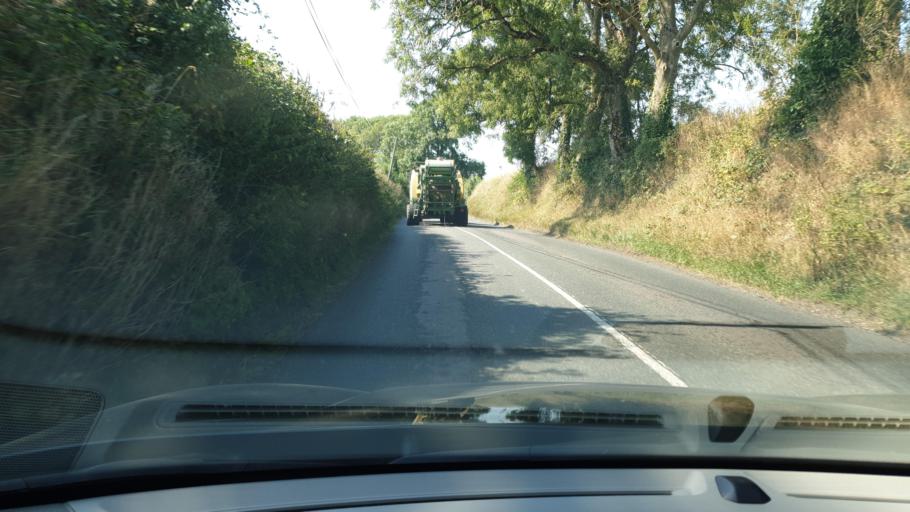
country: IE
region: Leinster
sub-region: An Mhi
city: Athboy
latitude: 53.5952
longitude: -6.8667
